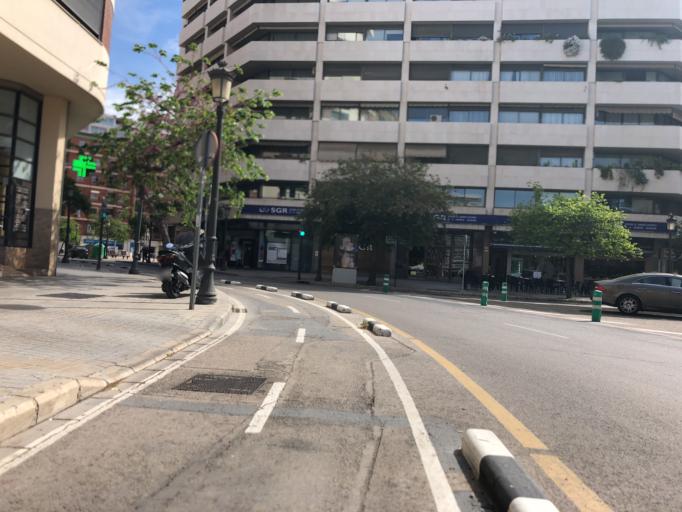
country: ES
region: Valencia
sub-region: Provincia de Valencia
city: Valencia
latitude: 39.4742
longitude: -0.3639
